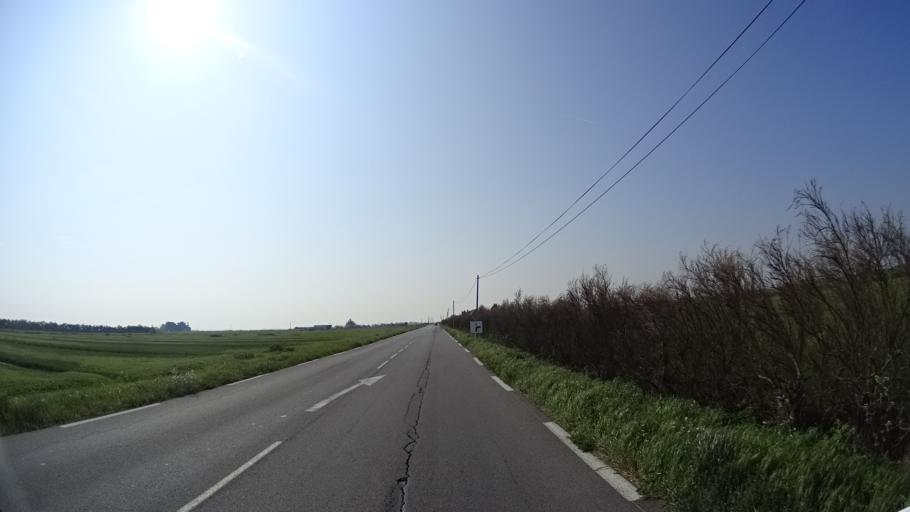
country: FR
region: Pays de la Loire
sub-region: Departement de la Loire-Atlantique
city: Bourgneuf-en-Retz
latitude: 47.0177
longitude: -1.9589
